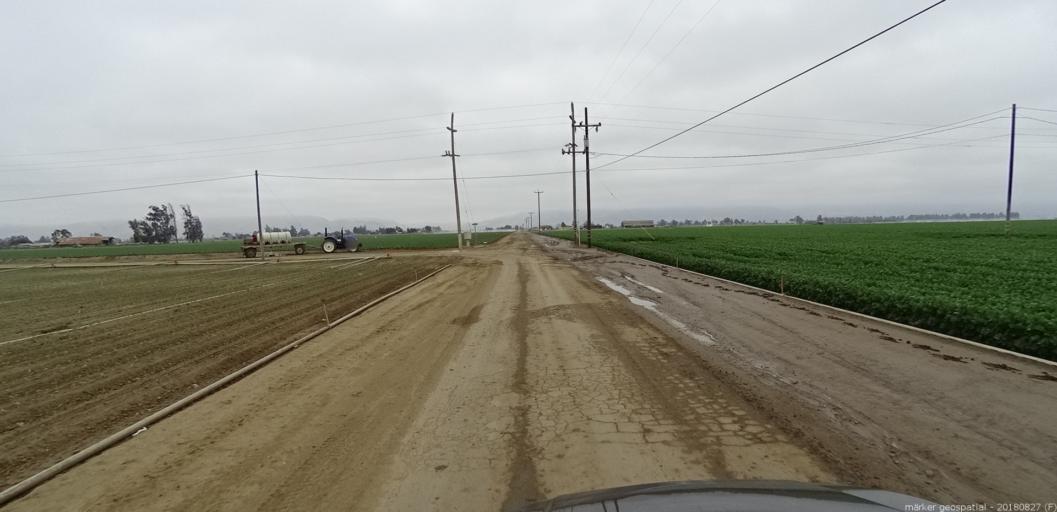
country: US
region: California
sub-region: Monterey County
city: Greenfield
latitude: 36.3423
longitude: -121.2365
